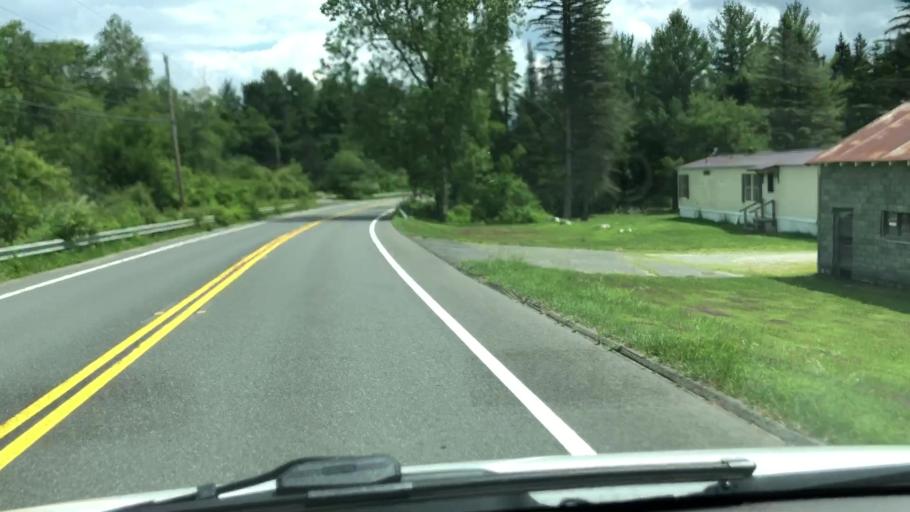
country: US
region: Massachusetts
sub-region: Berkshire County
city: Adams
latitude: 42.5749
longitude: -73.0487
